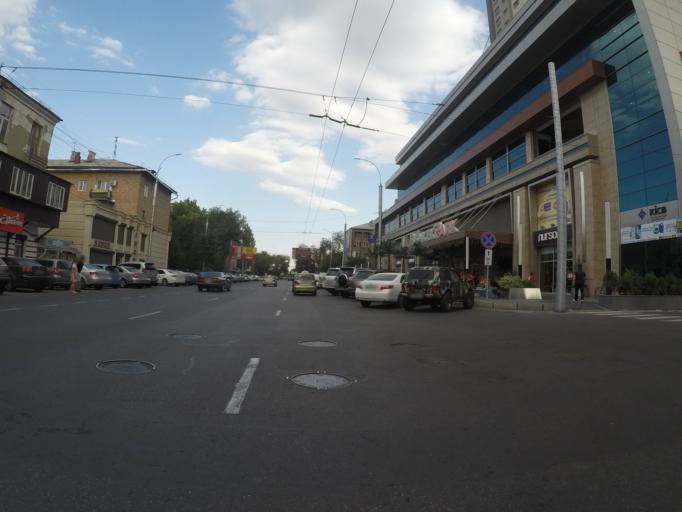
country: KG
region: Chuy
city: Bishkek
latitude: 42.8752
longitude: 74.5898
